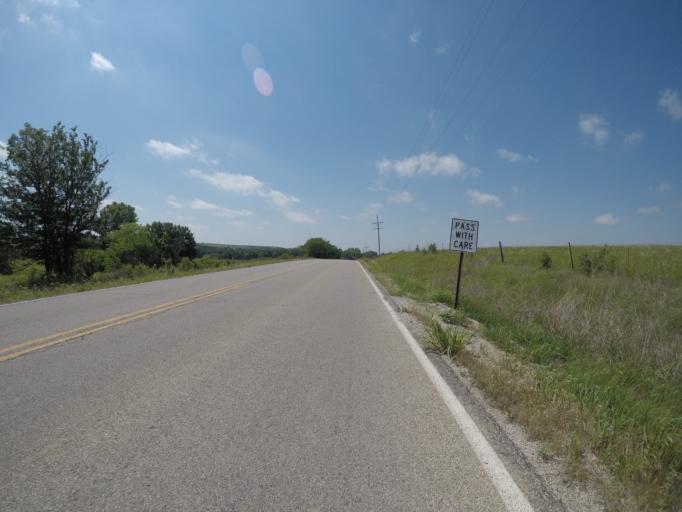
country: US
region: Kansas
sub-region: Pottawatomie County
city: Westmoreland
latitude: 39.3691
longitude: -96.4268
